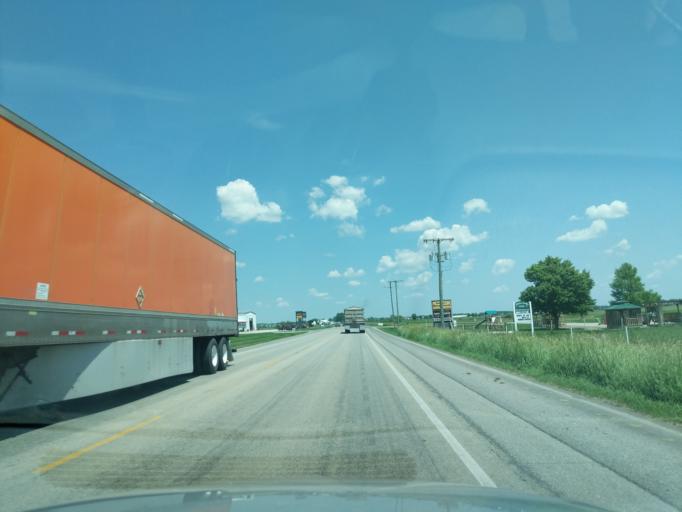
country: US
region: Indiana
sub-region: LaGrange County
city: Topeka
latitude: 41.5814
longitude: -85.5786
